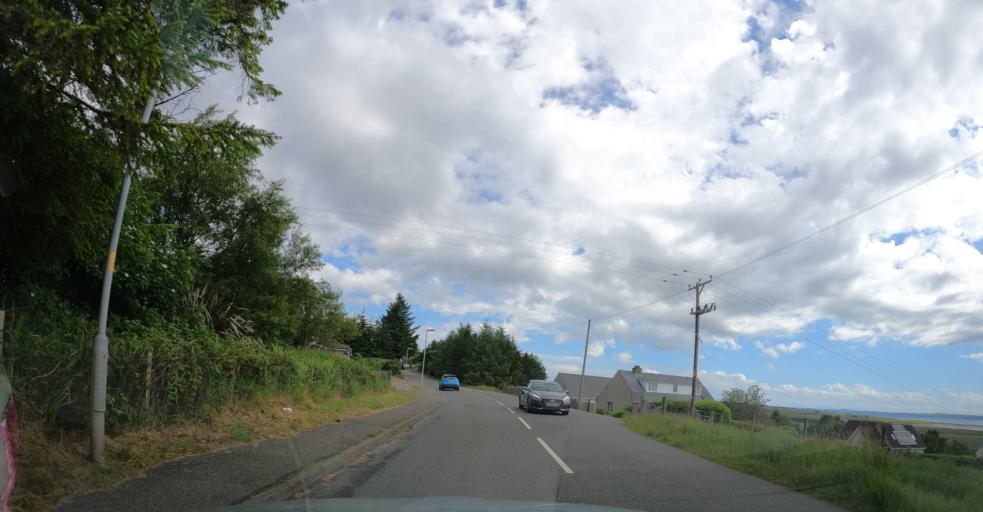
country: GB
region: Scotland
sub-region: Eilean Siar
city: Isle of Lewis
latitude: 58.2359
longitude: -6.3890
